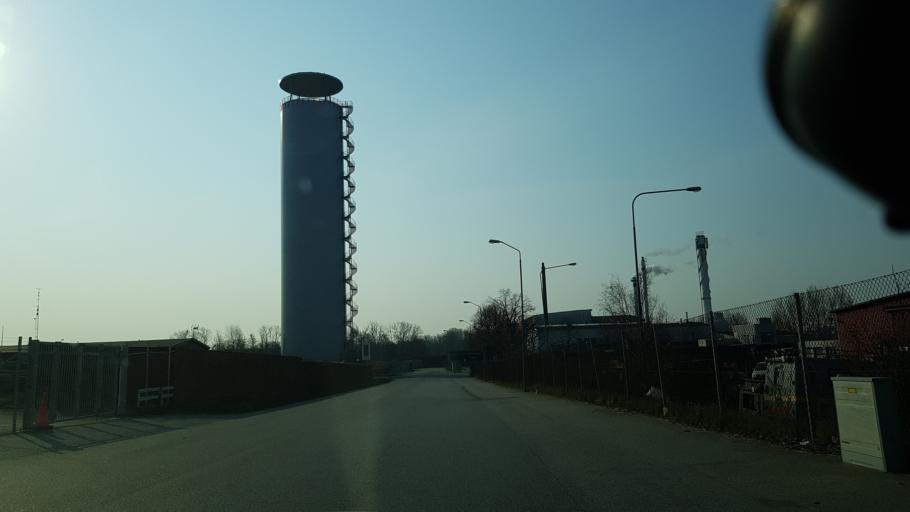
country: SE
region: Skane
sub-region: Ystads Kommun
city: Ystad
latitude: 55.4422
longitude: 13.8412
